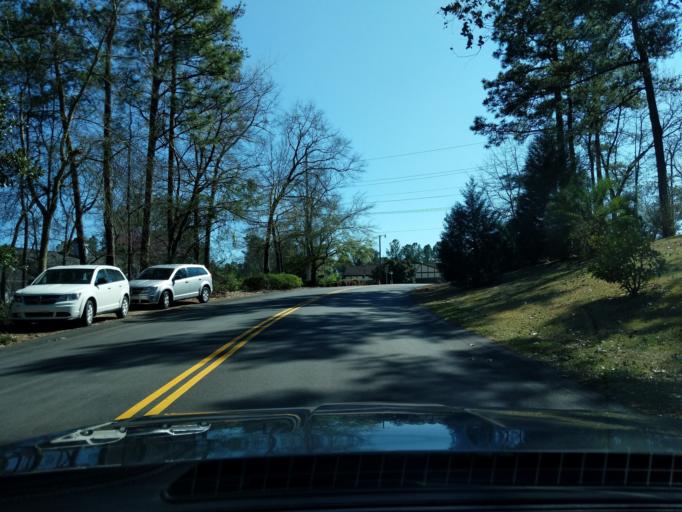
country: US
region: South Carolina
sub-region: Aiken County
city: Aiken
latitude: 33.5302
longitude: -81.7445
